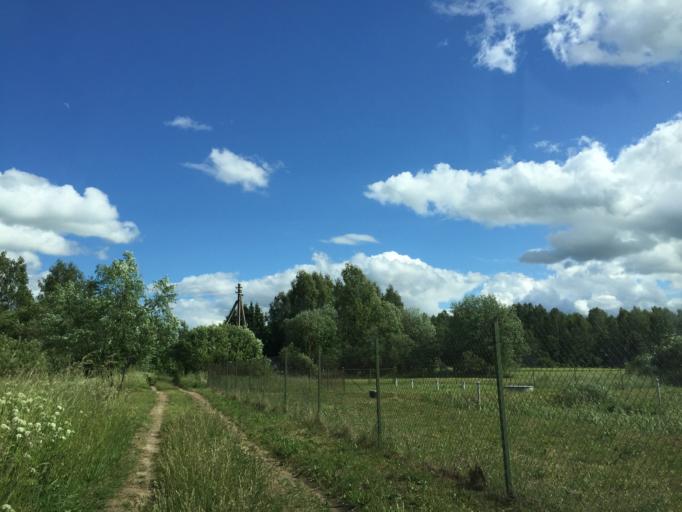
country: LT
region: Panevezys
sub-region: Birzai
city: Birzai
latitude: 56.3749
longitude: 24.6351
